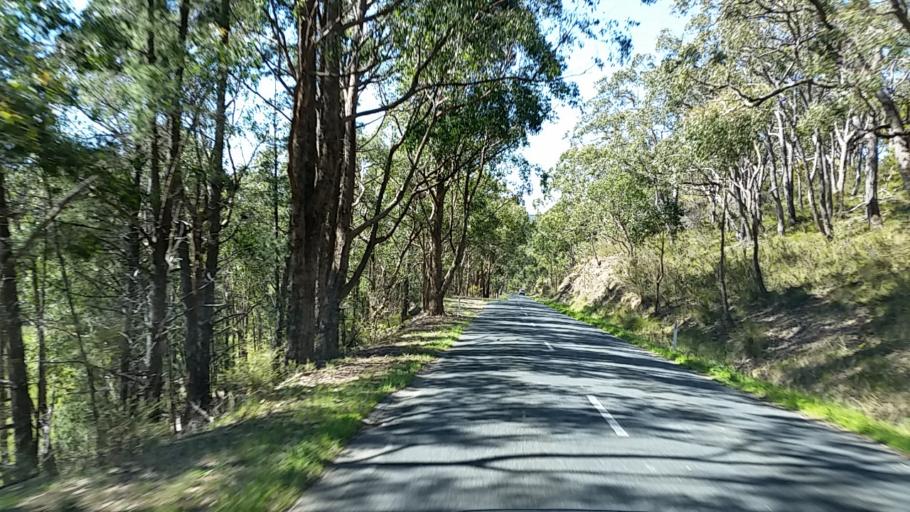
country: AU
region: South Australia
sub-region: Adelaide Hills
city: Bridgewater
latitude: -34.9501
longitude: 138.7621
